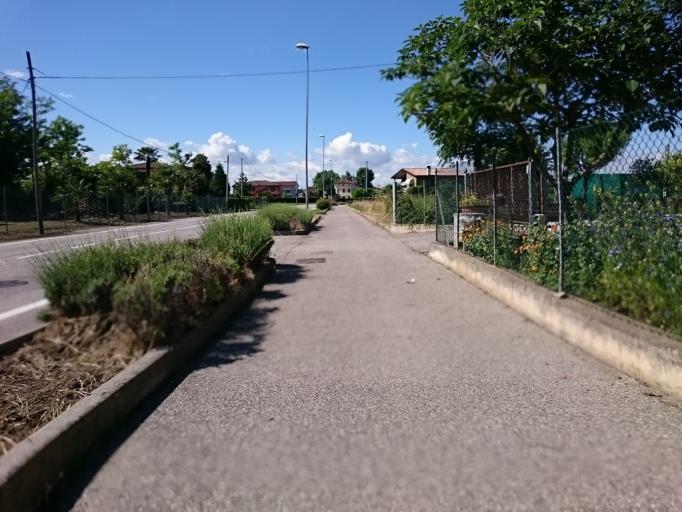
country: IT
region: Veneto
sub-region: Provincia di Venezia
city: Campolongo Maggiore Liettoli
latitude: 45.3307
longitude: 12.0212
